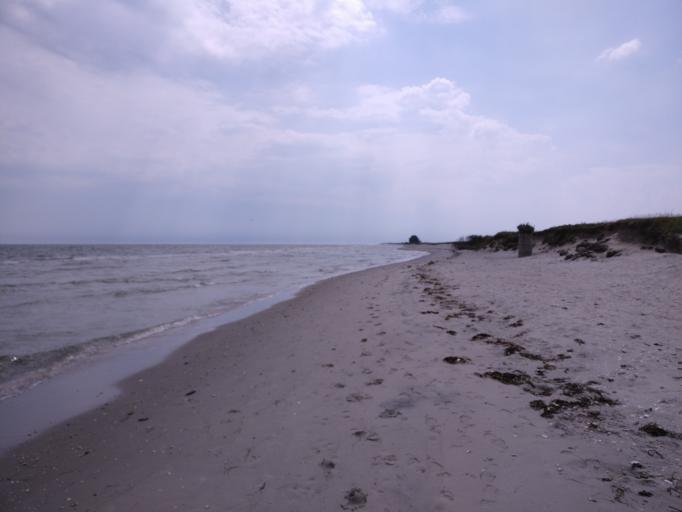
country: DK
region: North Denmark
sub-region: Frederikshavn Kommune
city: Saeby
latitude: 57.2450
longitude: 10.5491
